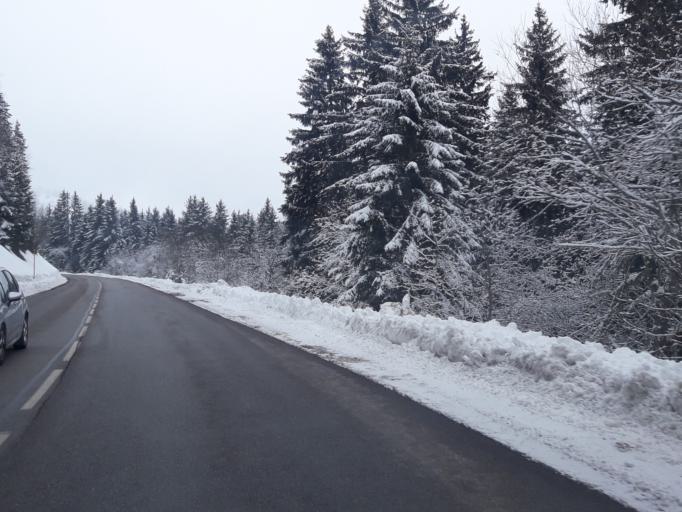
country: FR
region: Rhone-Alpes
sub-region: Departement de l'Isere
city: Theys
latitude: 45.2682
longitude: 6.0122
